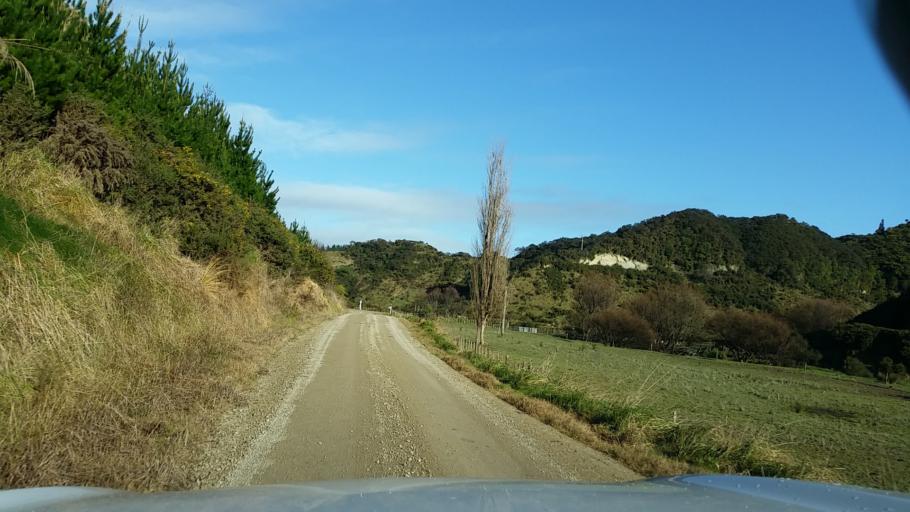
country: NZ
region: Taranaki
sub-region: South Taranaki District
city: Patea
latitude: -39.6962
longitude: 174.7425
